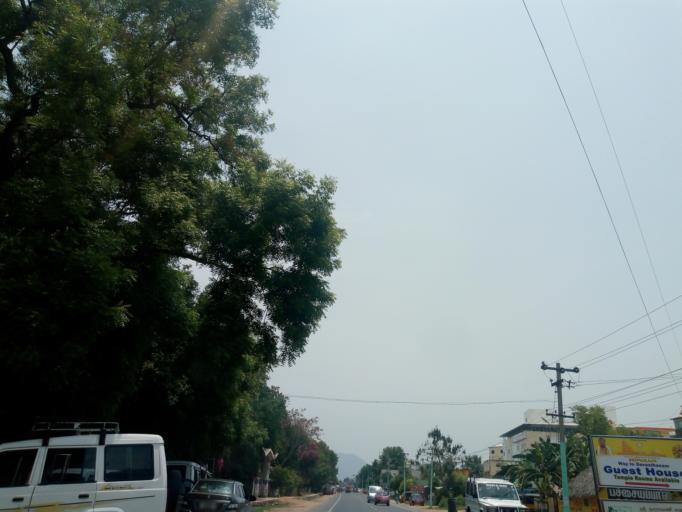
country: IN
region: Tamil Nadu
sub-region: Vellore
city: Vellore
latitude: 12.8706
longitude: 79.0924
